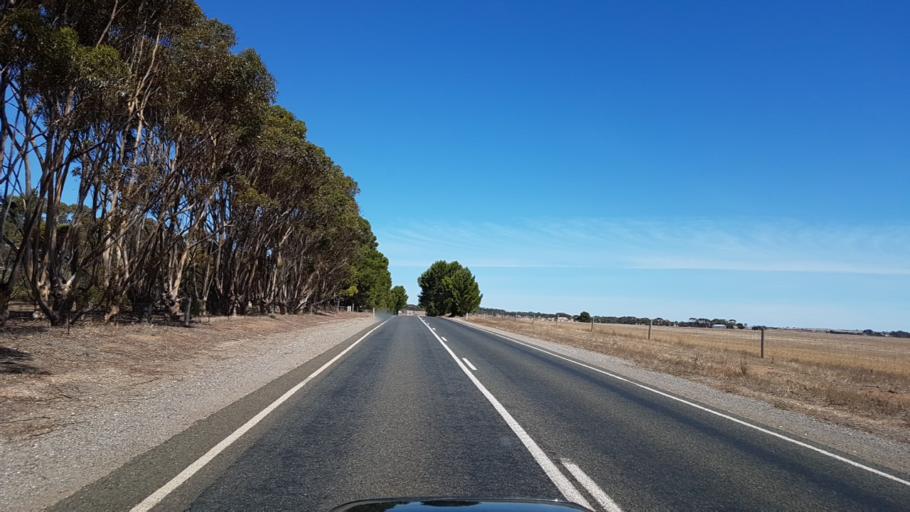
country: AU
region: South Australia
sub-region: Yorke Peninsula
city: Maitland
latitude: -34.3493
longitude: 137.6617
